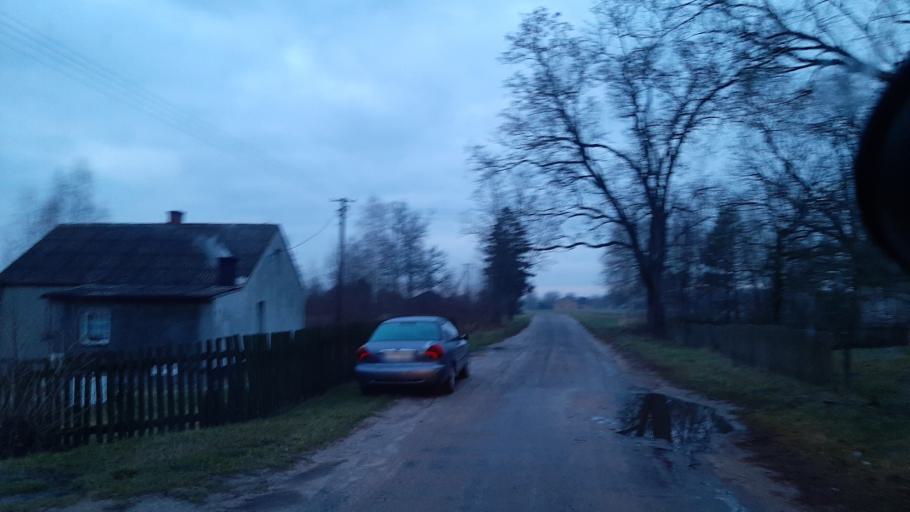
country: PL
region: Lublin Voivodeship
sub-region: Powiat lubartowski
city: Firlej
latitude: 51.5929
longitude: 22.5281
